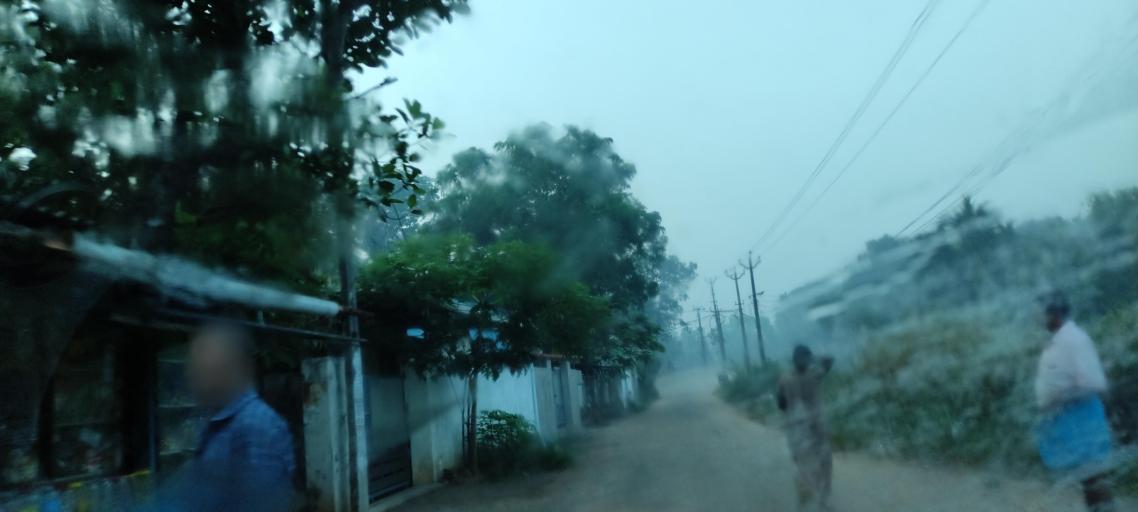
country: IN
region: Kerala
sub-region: Alappuzha
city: Alleppey
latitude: 9.5264
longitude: 76.3293
